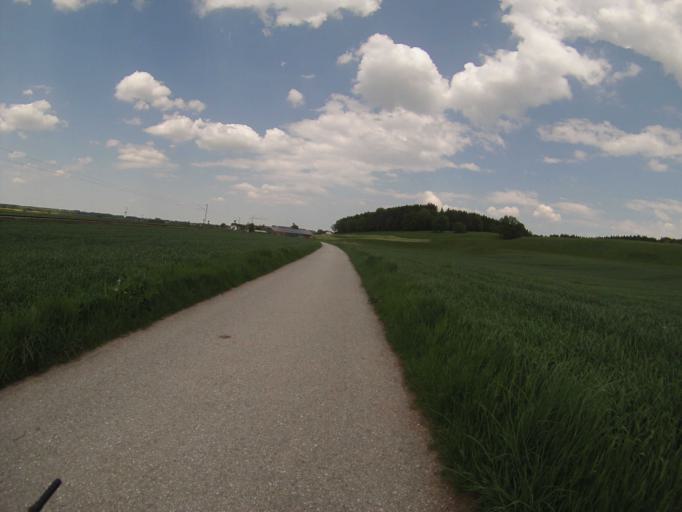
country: DE
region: Bavaria
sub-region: Upper Bavaria
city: Aying
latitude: 47.9548
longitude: 11.7797
